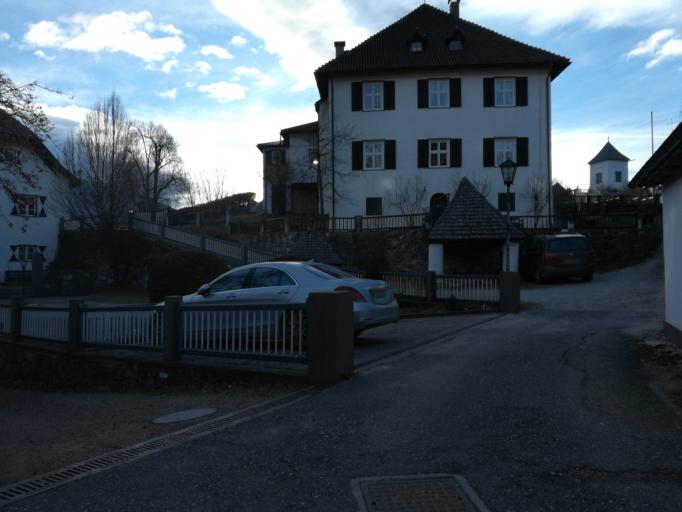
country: IT
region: Trentino-Alto Adige
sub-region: Bolzano
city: Collalbo
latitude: 46.5375
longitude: 11.4655
